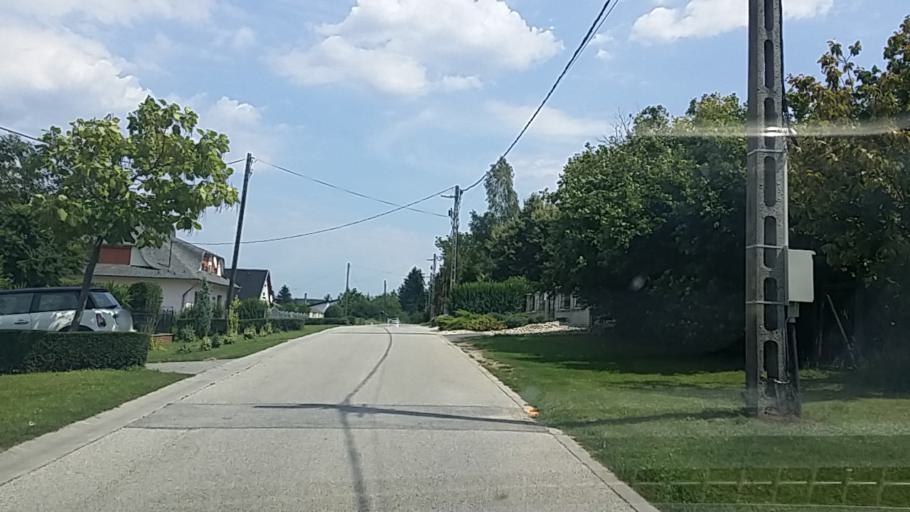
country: HU
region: Zala
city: Nagykanizsa
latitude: 46.4661
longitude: 17.0279
